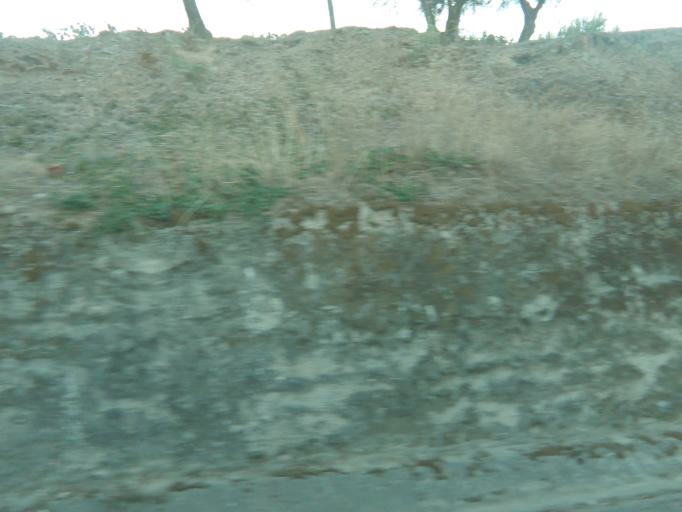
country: PT
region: Vila Real
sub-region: Peso da Regua
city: Godim
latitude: 41.1660
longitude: -7.8098
